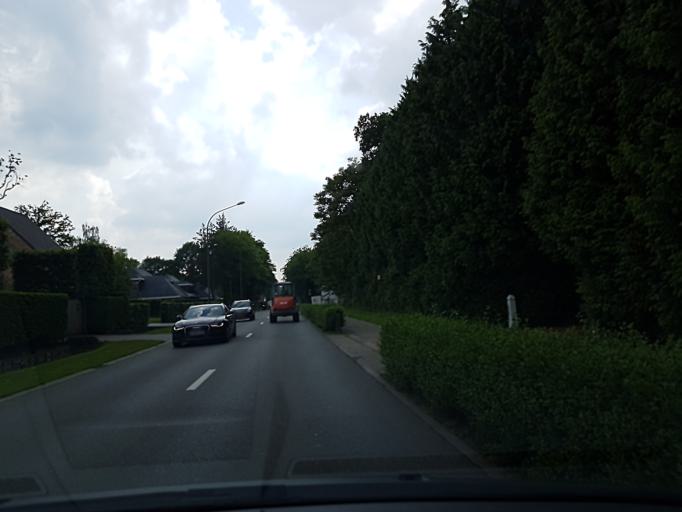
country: BE
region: Flanders
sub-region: Provincie Antwerpen
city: Schilde
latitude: 51.2577
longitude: 4.5482
